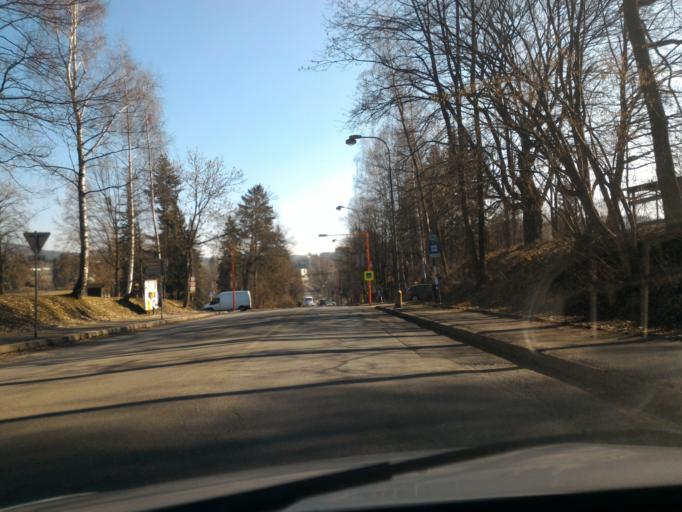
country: CZ
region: Liberecky
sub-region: Okres Jablonec nad Nisou
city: Jablonec nad Nisou
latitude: 50.7315
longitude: 15.1703
